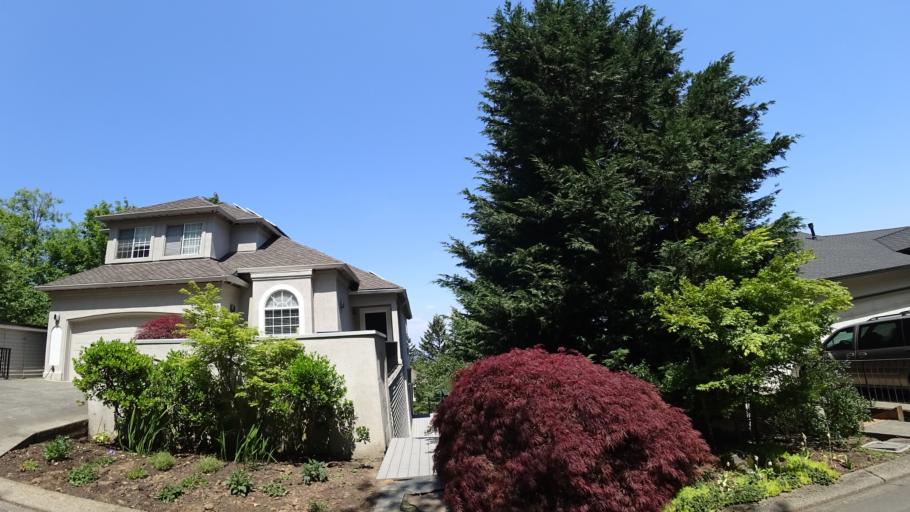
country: US
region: Oregon
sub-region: Washington County
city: Metzger
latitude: 45.4397
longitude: -122.7203
